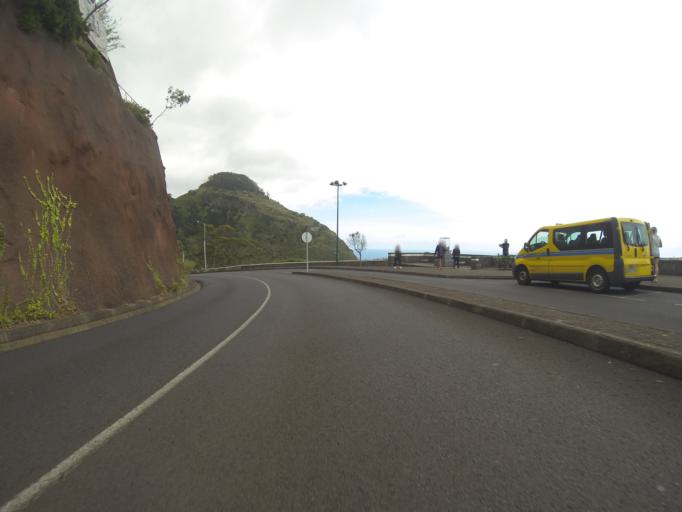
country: PT
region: Madeira
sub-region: Porto Moniz
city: Porto Moniz
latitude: 32.8624
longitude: -17.1766
